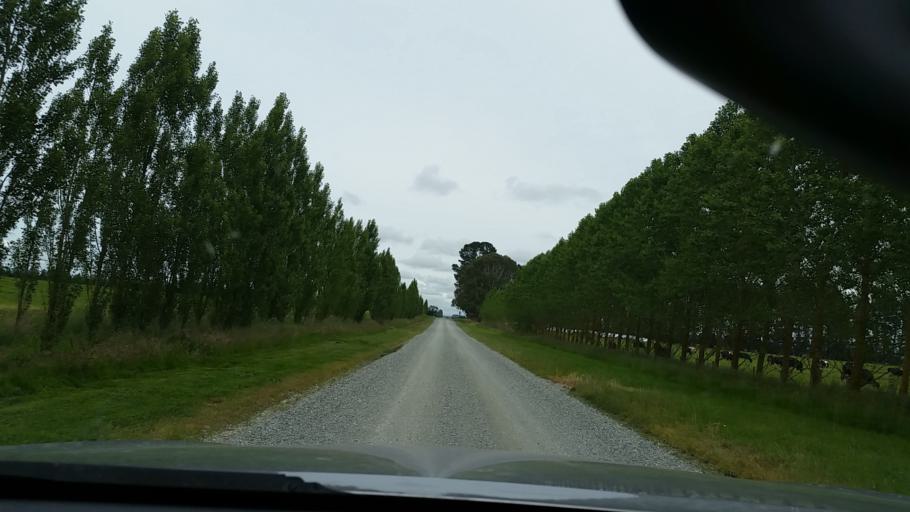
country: NZ
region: Southland
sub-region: Gore District
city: Gore
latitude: -45.7918
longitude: 168.7147
